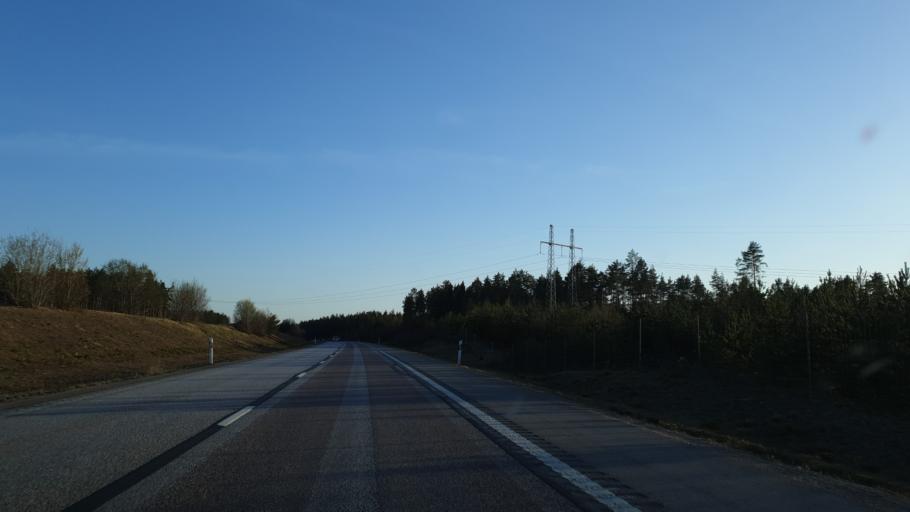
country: SE
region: Uppsala
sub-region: Tierps Kommun
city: Tierp
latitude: 60.2891
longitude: 17.5076
